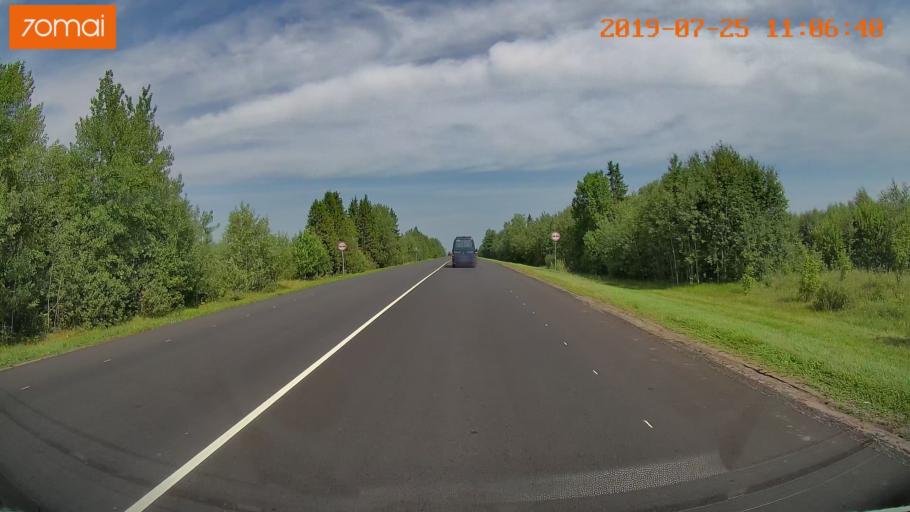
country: RU
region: Ivanovo
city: Furmanov
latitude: 57.2579
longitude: 41.1566
